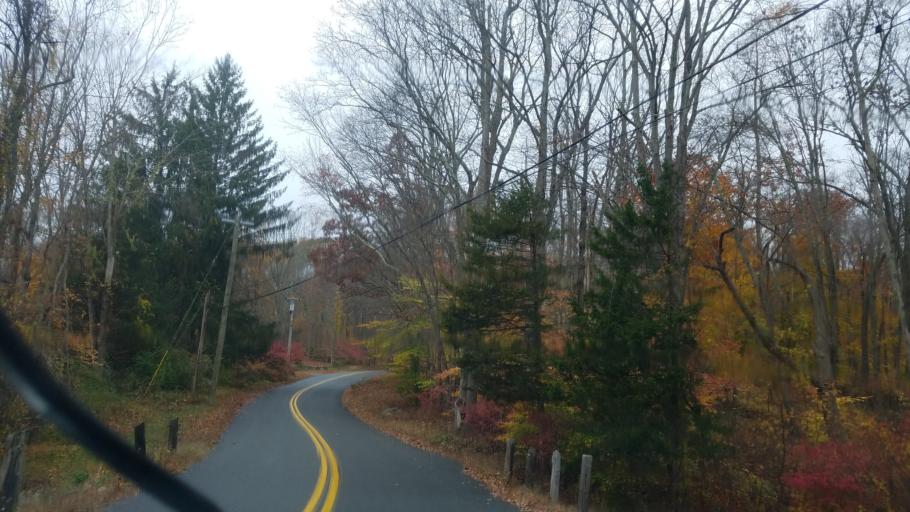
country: US
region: Connecticut
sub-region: Middlesex County
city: Higganum
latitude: 41.5173
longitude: -72.5288
